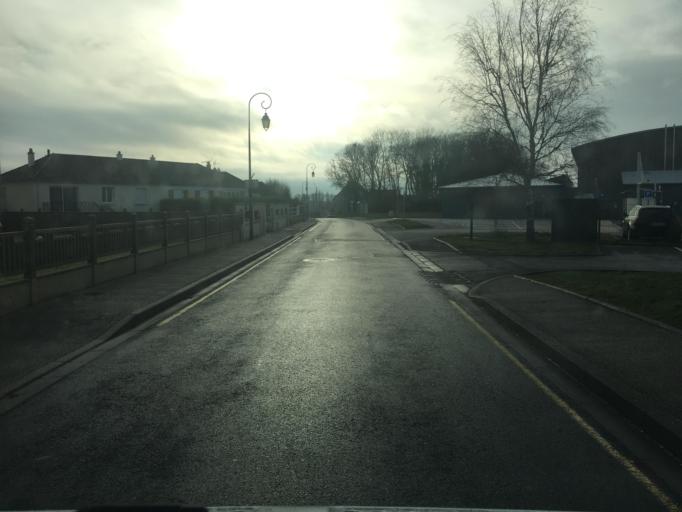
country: FR
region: Lower Normandy
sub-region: Departement du Calvados
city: Rots
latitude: 49.2044
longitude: -0.4762
